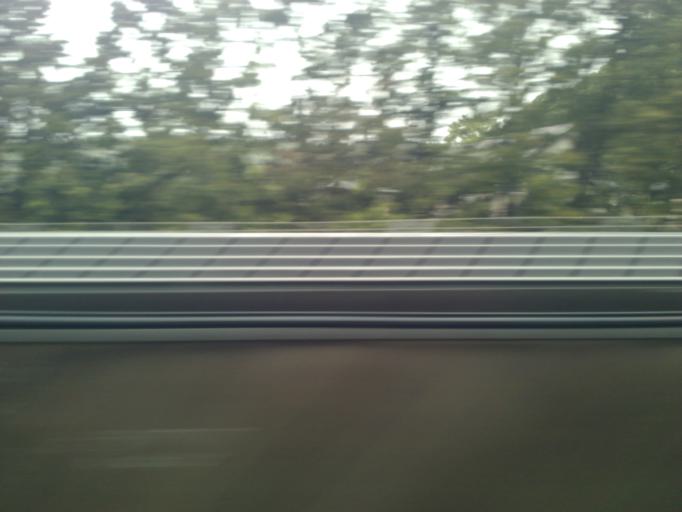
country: JP
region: Kanagawa
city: Ninomiya
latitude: 35.3122
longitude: 139.2630
